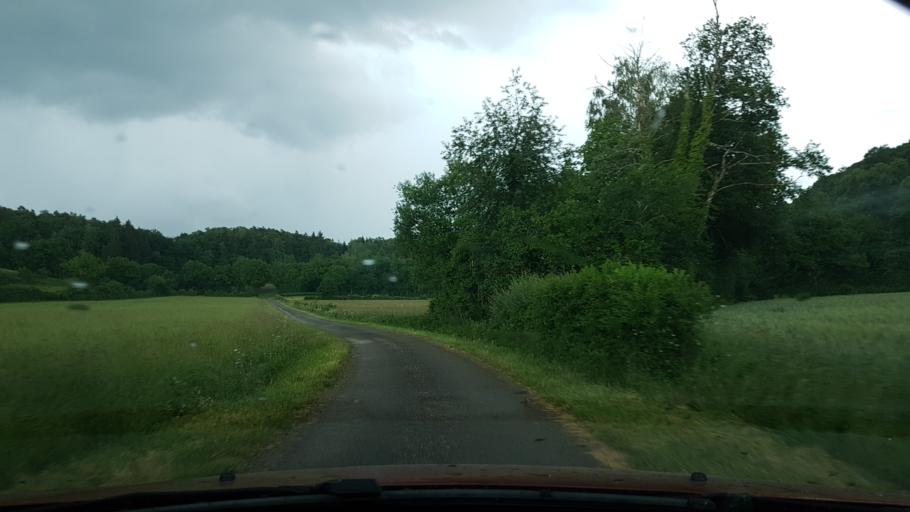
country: FR
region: Franche-Comte
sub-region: Departement du Jura
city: Clairvaux-les-Lacs
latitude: 46.5377
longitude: 5.7040
